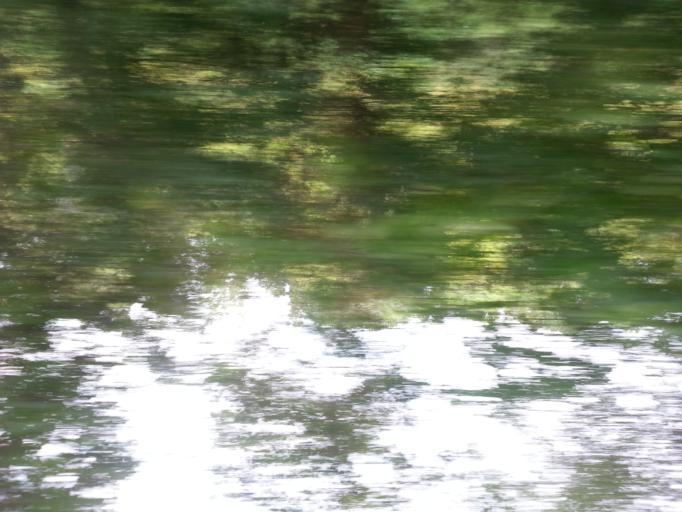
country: US
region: Tennessee
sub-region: Dickson County
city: Burns
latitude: 36.0312
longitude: -87.3207
